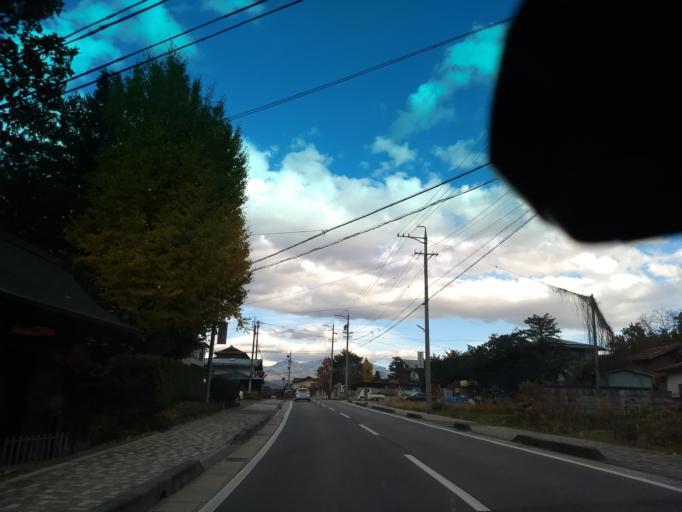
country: JP
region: Nagano
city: Chino
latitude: 35.9964
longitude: 138.1256
